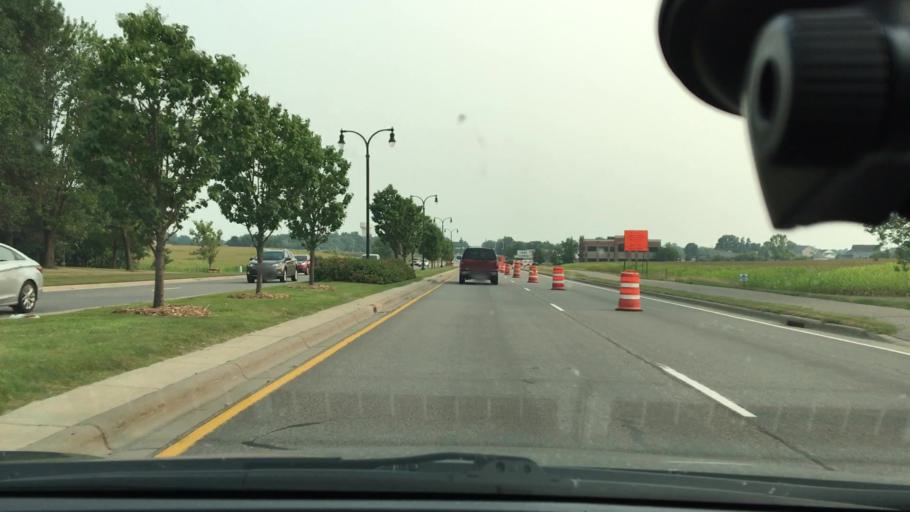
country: US
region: Minnesota
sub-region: Wright County
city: Albertville
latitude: 45.2314
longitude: -93.6644
